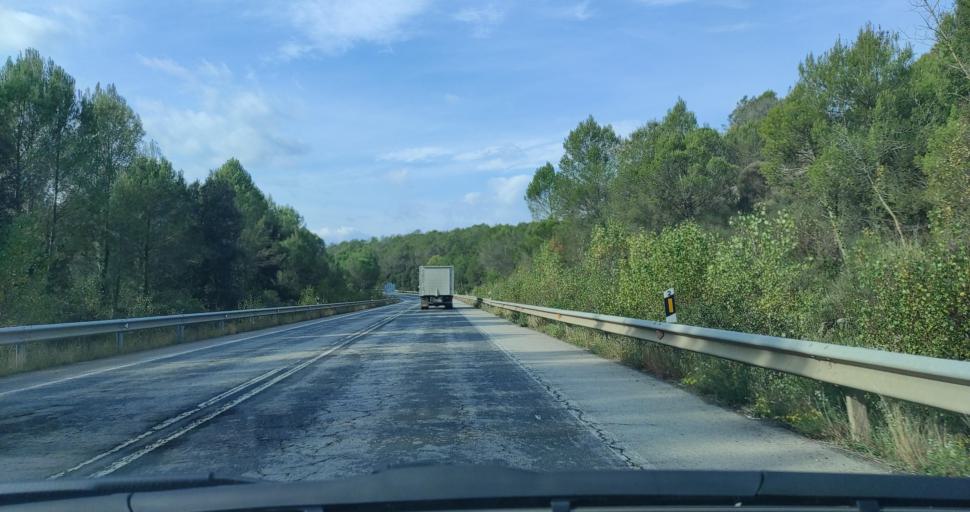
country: ES
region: Catalonia
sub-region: Provincia de Girona
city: Crespia
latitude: 42.2089
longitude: 2.7949
